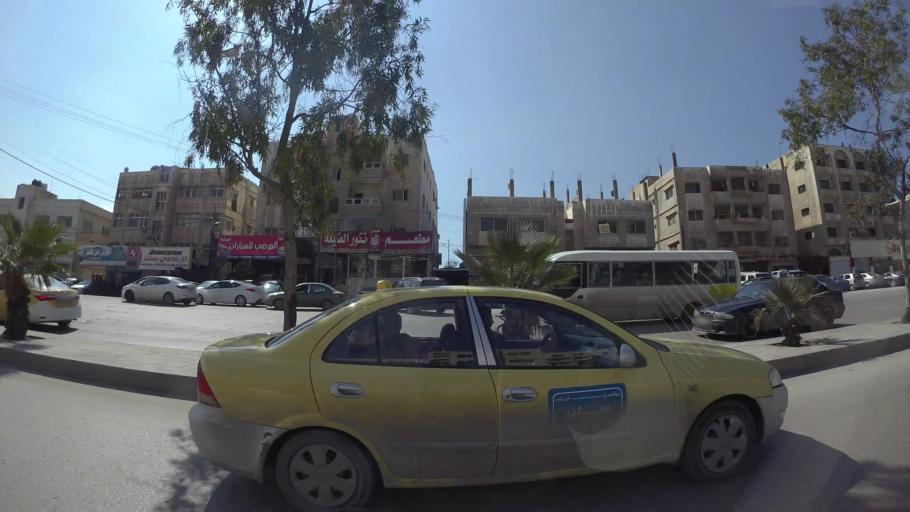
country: JO
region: Zarqa
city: Zarqa
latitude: 32.0468
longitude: 36.0926
